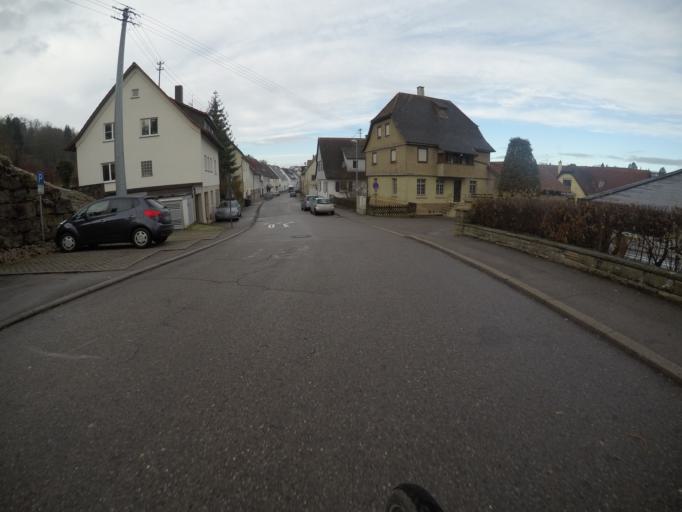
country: DE
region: Baden-Wuerttemberg
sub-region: Regierungsbezirk Stuttgart
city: Aidlingen
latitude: 48.6771
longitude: 8.8968
